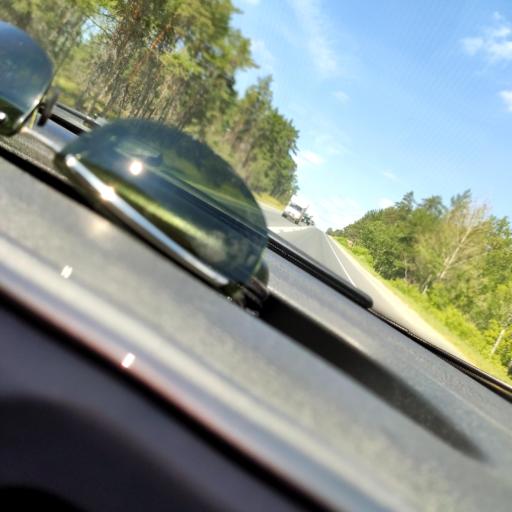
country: RU
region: Samara
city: Volzhskiy
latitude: 53.4411
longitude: 50.1064
